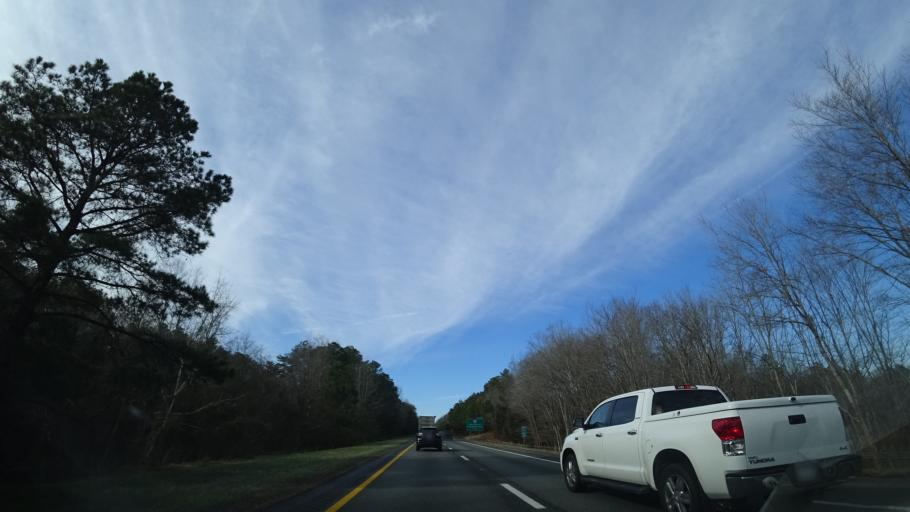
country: US
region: Virginia
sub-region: New Kent County
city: New Kent
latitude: 37.4905
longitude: -76.9967
